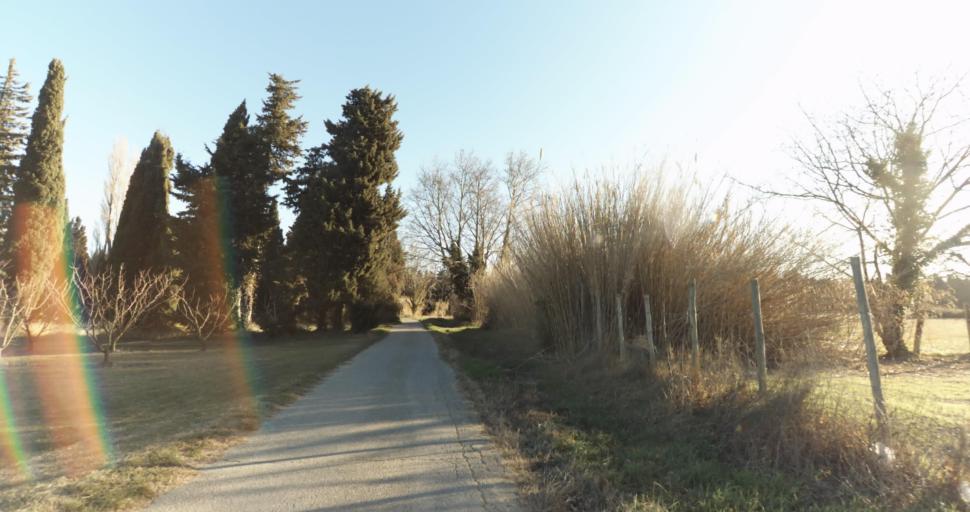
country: FR
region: Provence-Alpes-Cote d'Azur
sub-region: Departement des Bouches-du-Rhone
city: Barbentane
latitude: 43.9185
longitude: 4.7518
